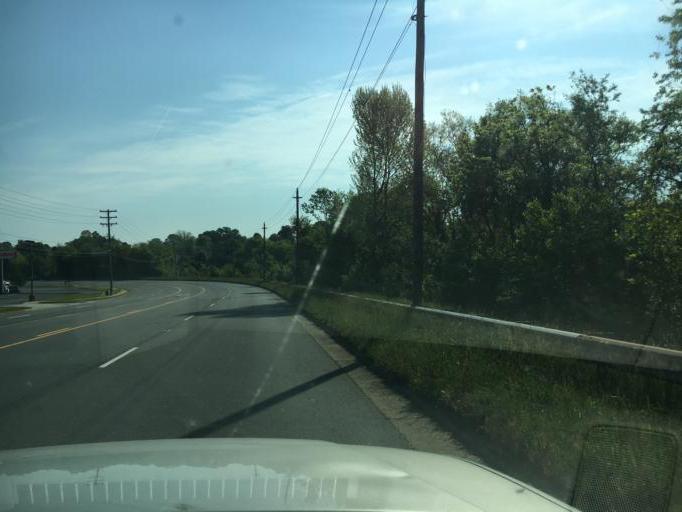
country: US
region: North Carolina
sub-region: Burke County
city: Morganton
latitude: 35.7356
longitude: -81.6815
